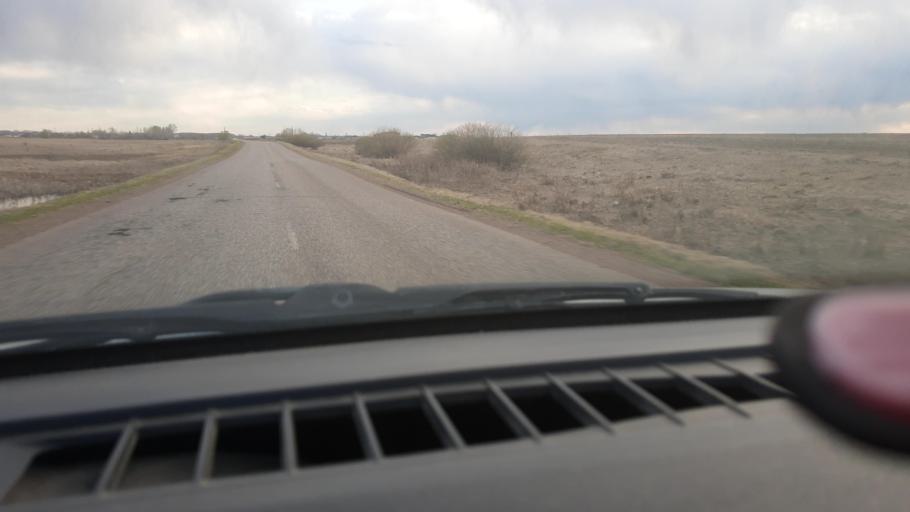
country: RU
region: Bashkortostan
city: Asanovo
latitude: 54.9197
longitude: 55.5091
